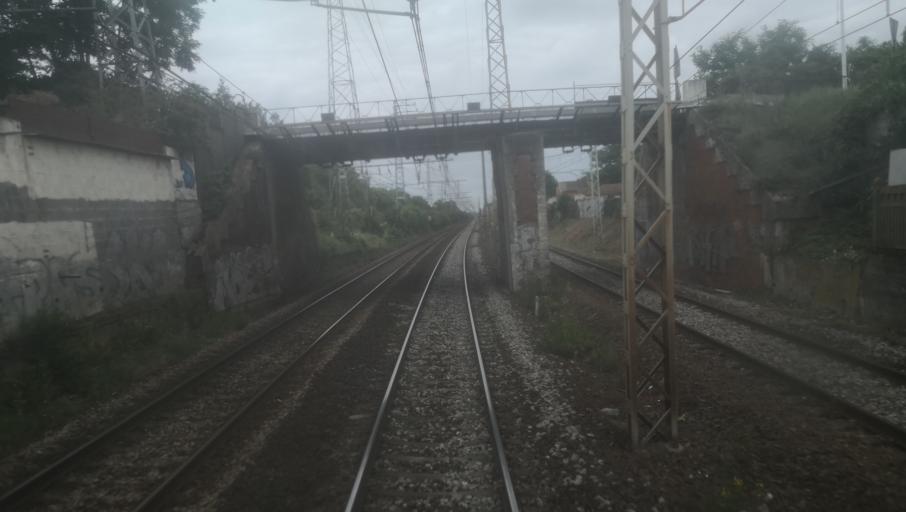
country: FR
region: Midi-Pyrenees
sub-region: Departement de la Haute-Garonne
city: Aucamville
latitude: 43.6674
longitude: 1.4110
